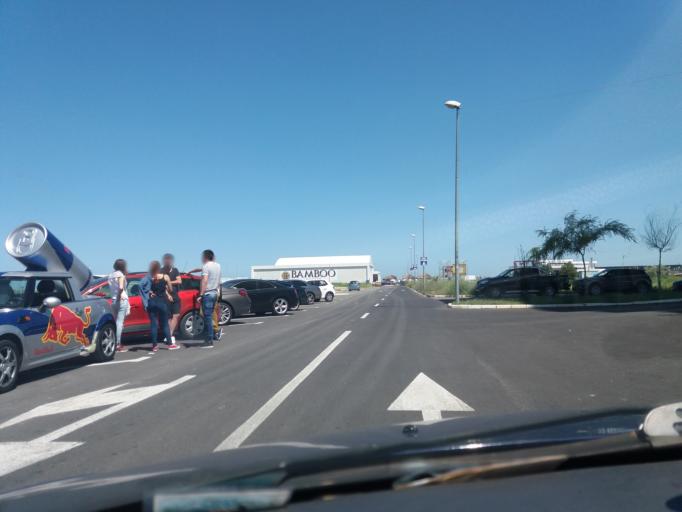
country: RO
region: Constanta
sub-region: Municipiul Constanta
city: Palazu Mare
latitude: 44.2709
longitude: 28.6177
